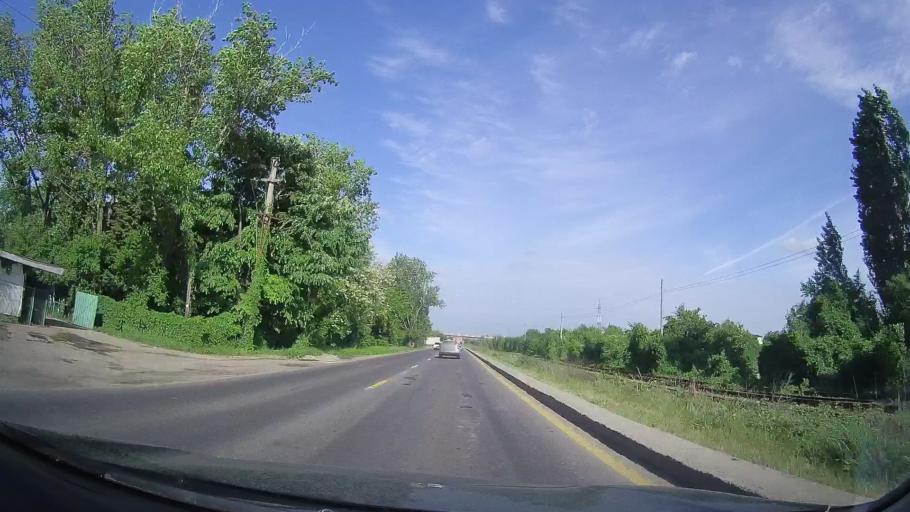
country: RO
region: Ilfov
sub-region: Comuna Magurele
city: Magurele
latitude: 44.3574
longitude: 26.0422
